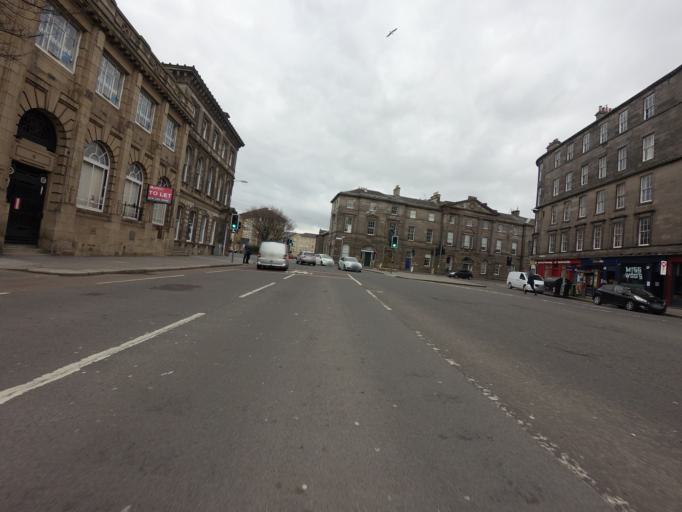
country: GB
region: Scotland
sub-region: West Lothian
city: Seafield
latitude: 55.9756
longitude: -3.1672
